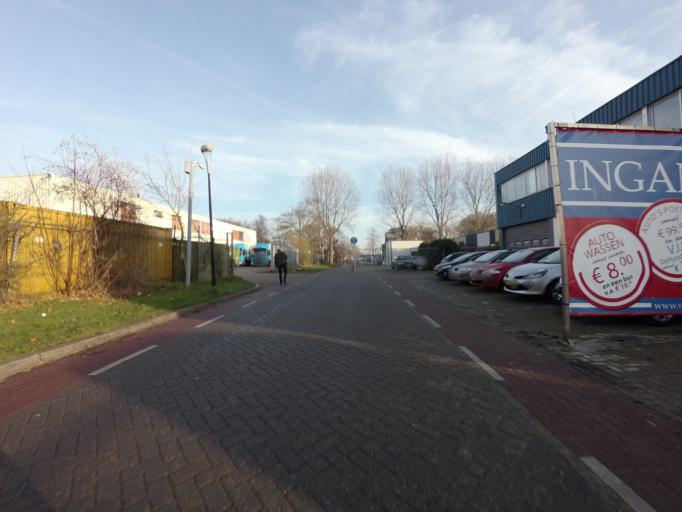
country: NL
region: Utrecht
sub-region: Gemeente De Ronde Venen
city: Mijdrecht
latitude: 52.2028
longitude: 4.8852
